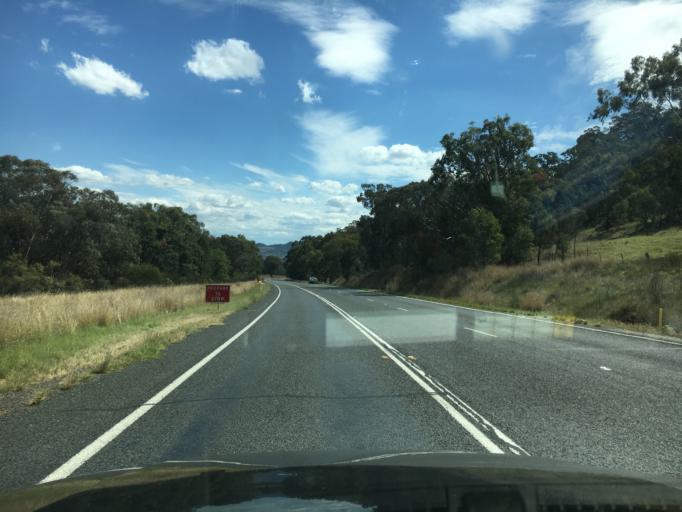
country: AU
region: New South Wales
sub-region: Liverpool Plains
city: Quirindi
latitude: -31.4461
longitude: 150.8723
